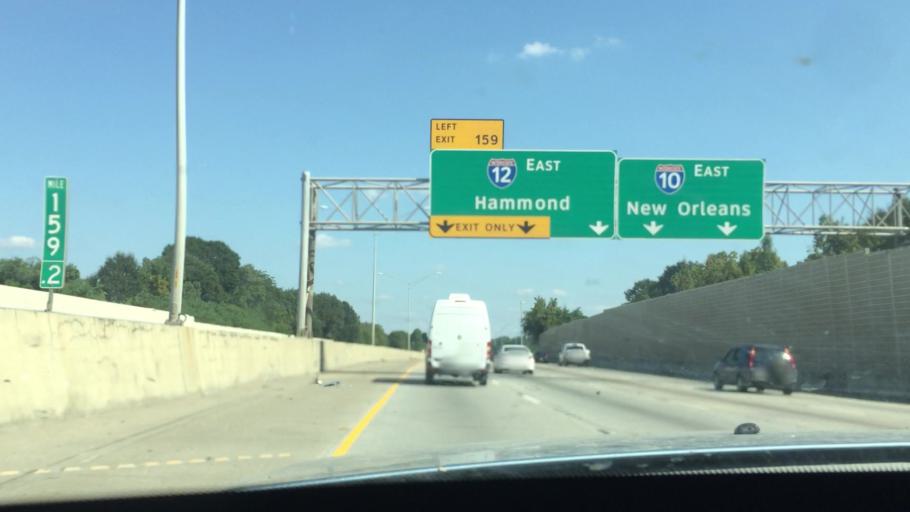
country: US
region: Louisiana
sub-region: East Baton Rouge Parish
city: Westminster
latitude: 30.4213
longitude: -91.1255
